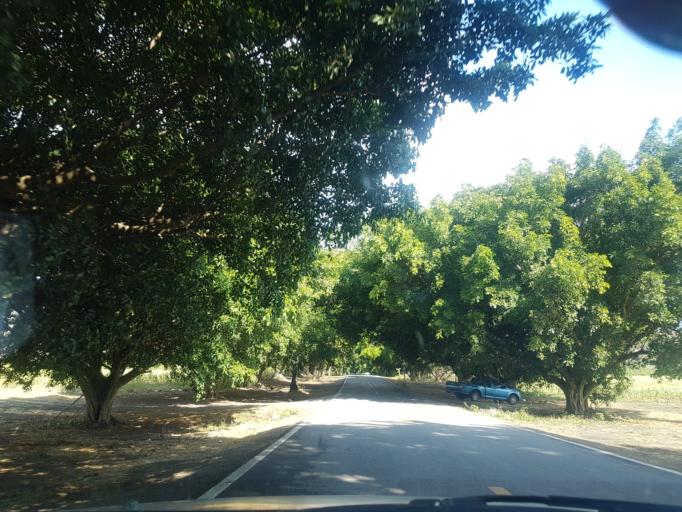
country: TH
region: Lop Buri
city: Lop Buri
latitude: 14.8148
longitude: 100.7518
